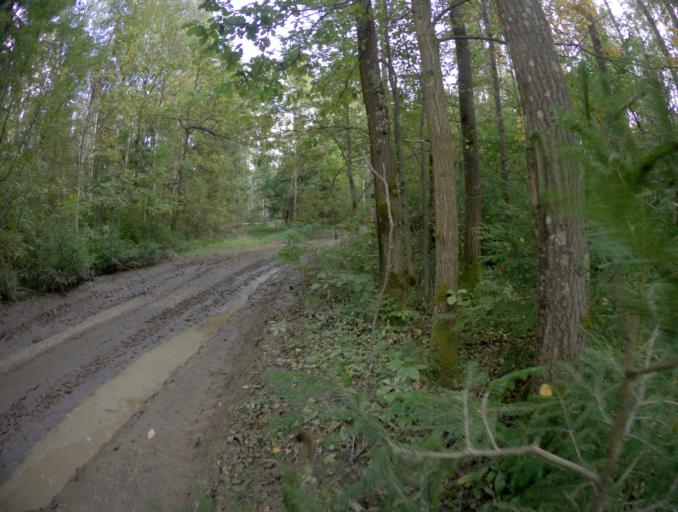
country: RU
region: Vladimir
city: Kommunar
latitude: 56.0327
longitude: 40.5142
